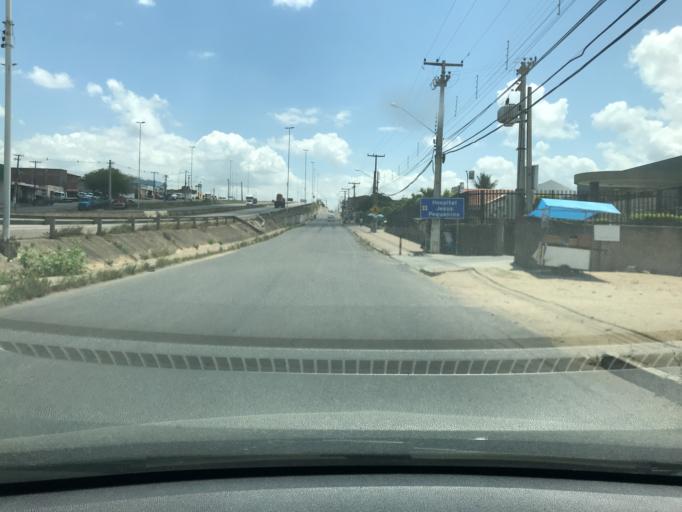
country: BR
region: Pernambuco
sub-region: Bezerros
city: Bezerros
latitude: -8.2451
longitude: -35.7557
